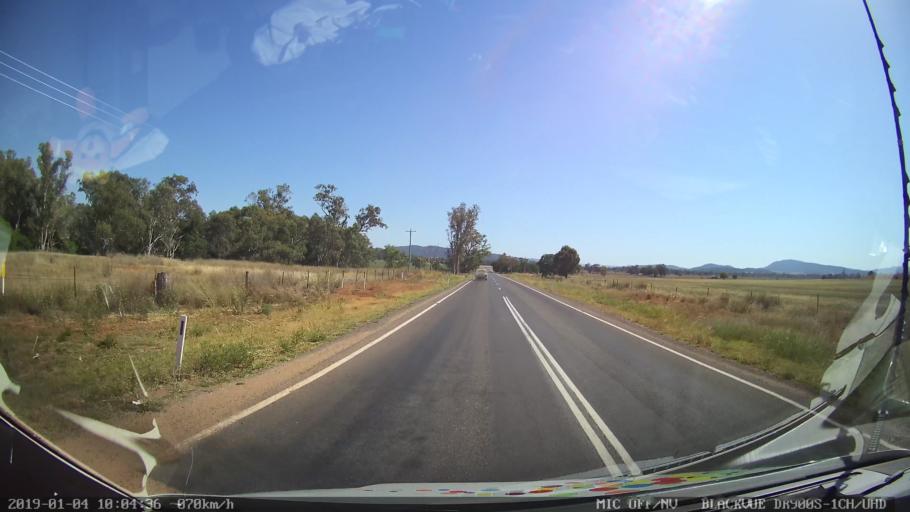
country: AU
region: New South Wales
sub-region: Cabonne
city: Canowindra
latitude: -33.4508
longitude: 148.3617
